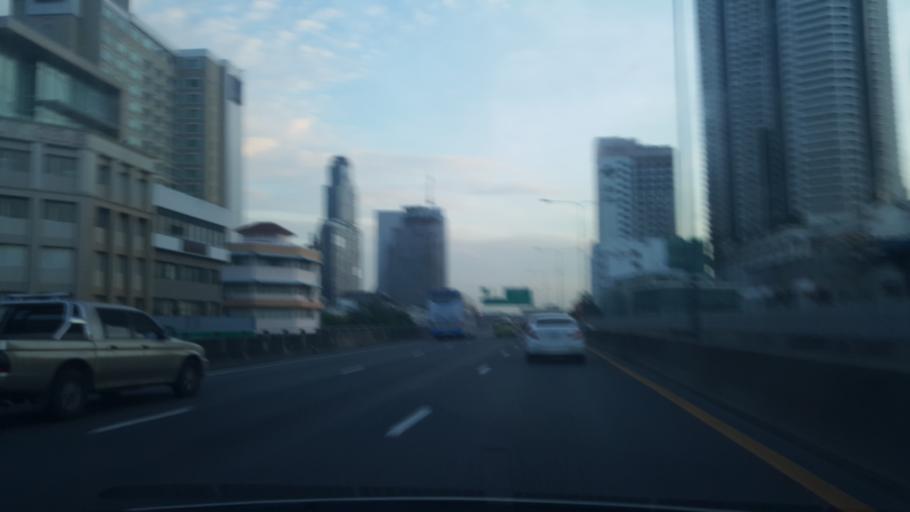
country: TH
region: Bangkok
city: Samphanthawong
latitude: 13.7242
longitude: 100.5176
